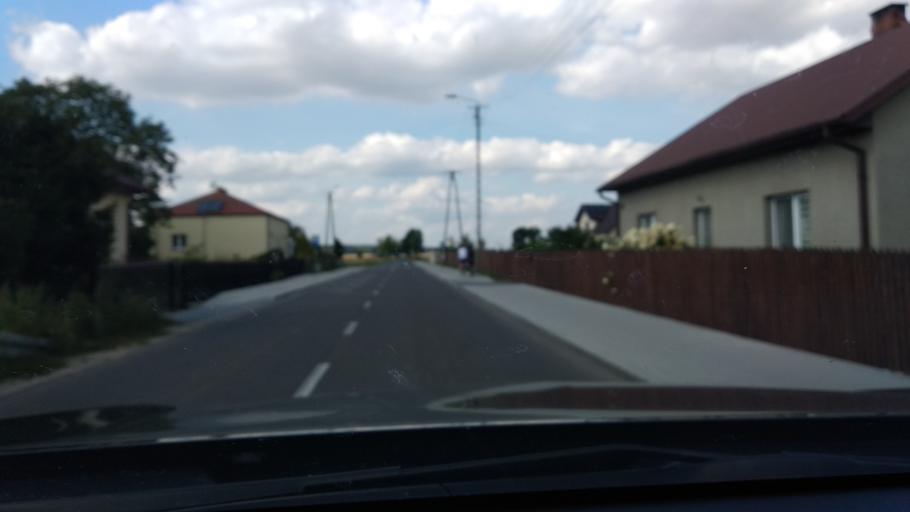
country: PL
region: Masovian Voivodeship
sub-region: Powiat pultuski
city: Zatory
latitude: 52.5607
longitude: 21.1871
